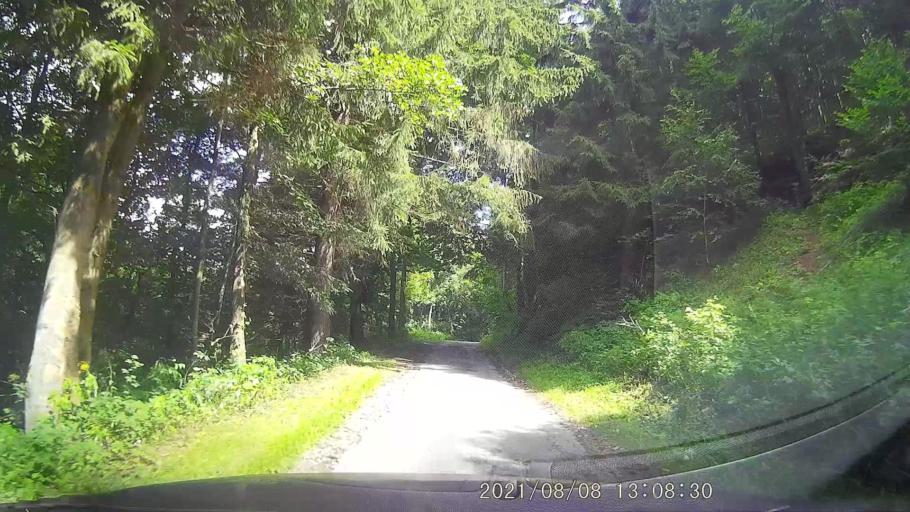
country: PL
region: Lower Silesian Voivodeship
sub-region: Powiat klodzki
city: Lewin Klodzki
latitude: 50.4367
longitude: 16.3038
